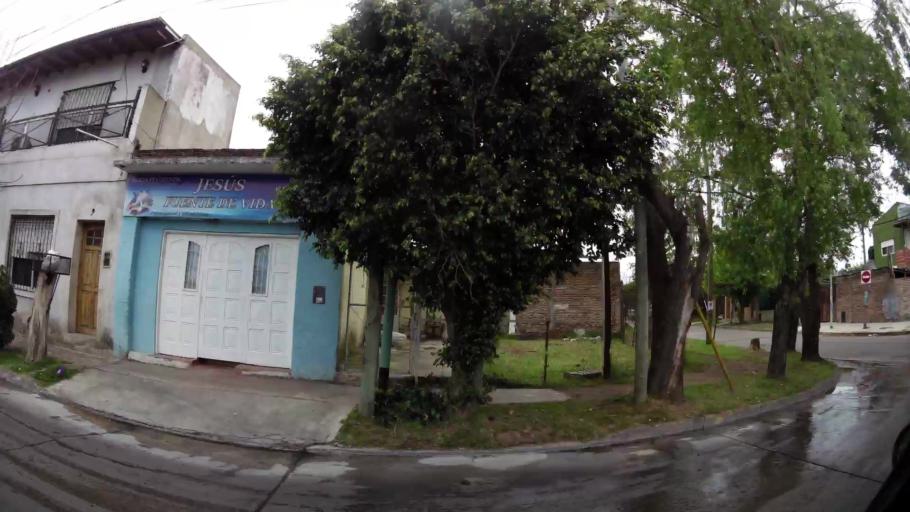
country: AR
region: Buenos Aires
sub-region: Partido de Quilmes
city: Quilmes
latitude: -34.7562
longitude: -58.2195
